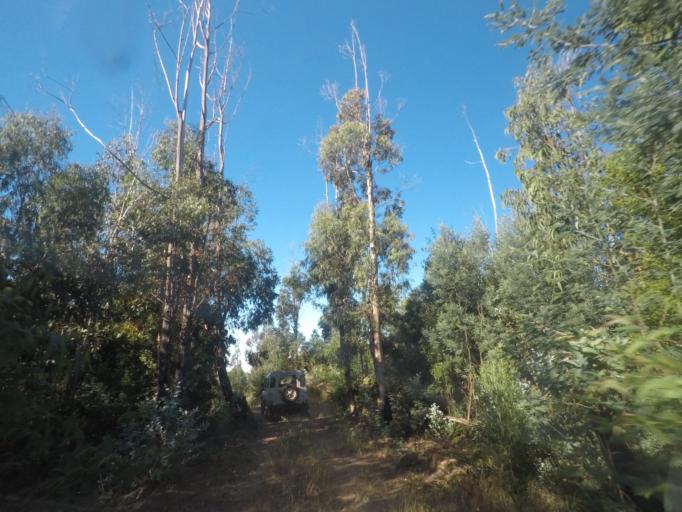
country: PT
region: Madeira
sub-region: Funchal
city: Nossa Senhora do Monte
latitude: 32.6927
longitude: -16.9128
